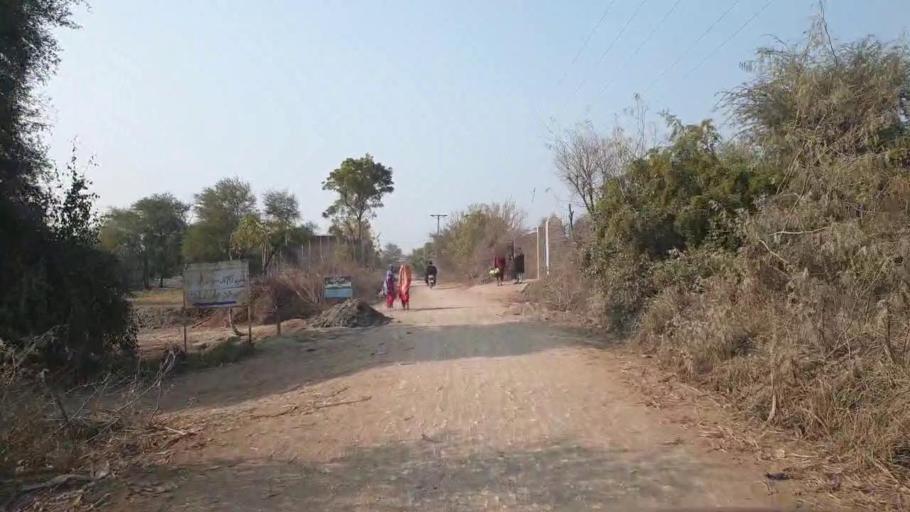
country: PK
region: Sindh
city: Bhit Shah
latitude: 25.8953
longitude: 68.4728
